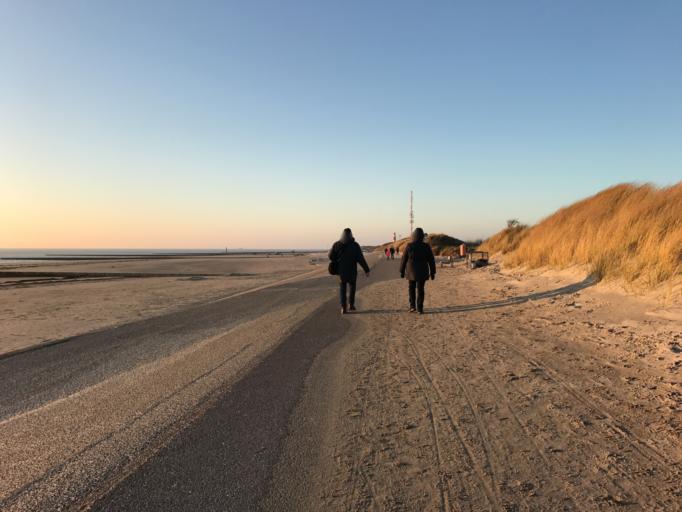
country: DE
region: Lower Saxony
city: Borkum
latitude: 53.5740
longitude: 6.6799
